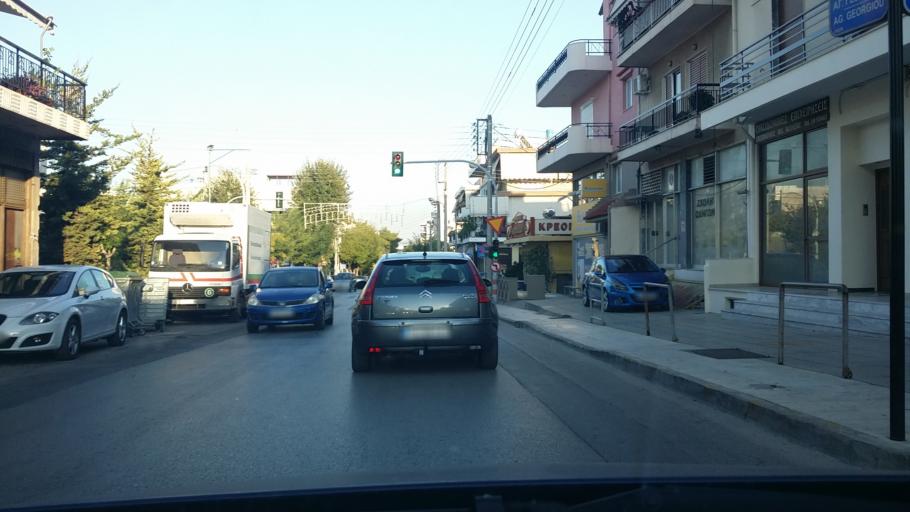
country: GR
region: Attica
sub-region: Nomarchia Athinas
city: Ilion
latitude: 38.0293
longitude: 23.6919
